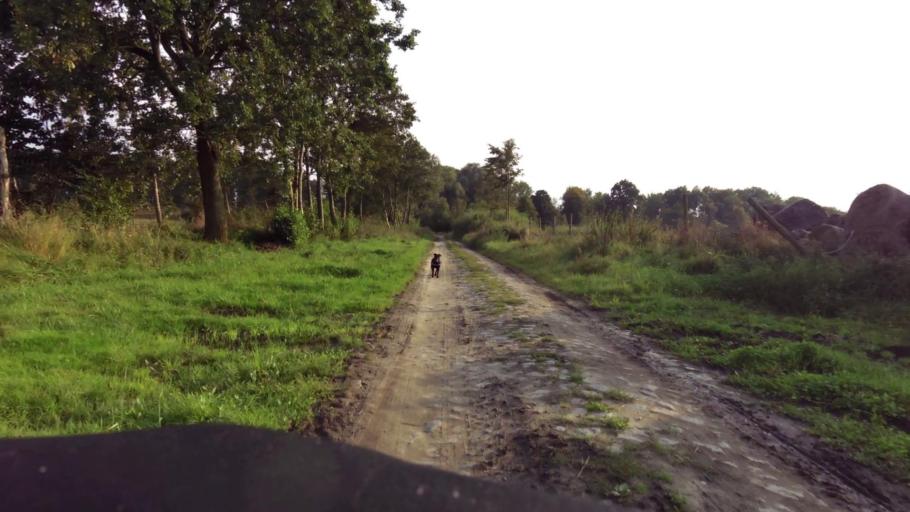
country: PL
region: West Pomeranian Voivodeship
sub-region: Powiat stargardzki
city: Suchan
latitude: 53.3335
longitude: 15.3645
